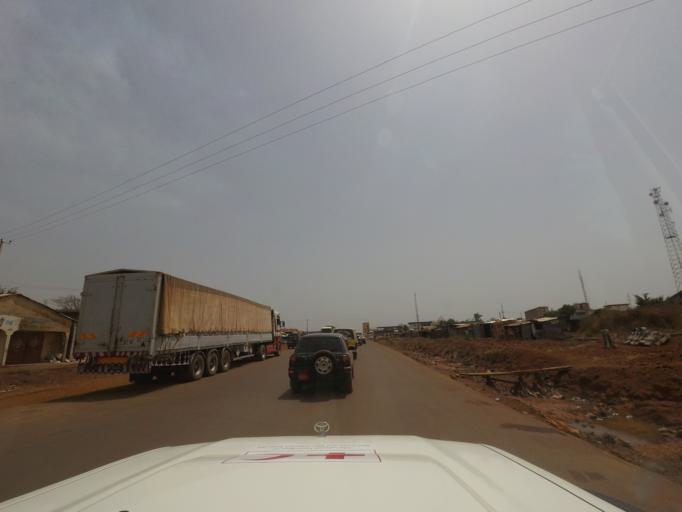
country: GN
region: Kindia
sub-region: Prefecture de Dubreka
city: Dubreka
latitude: 9.7203
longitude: -13.4809
